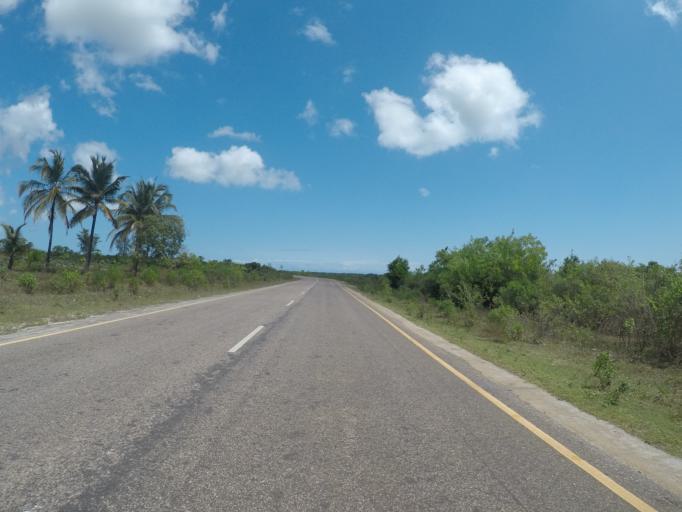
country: TZ
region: Zanzibar Central/South
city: Koani
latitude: -6.2472
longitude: 39.3551
